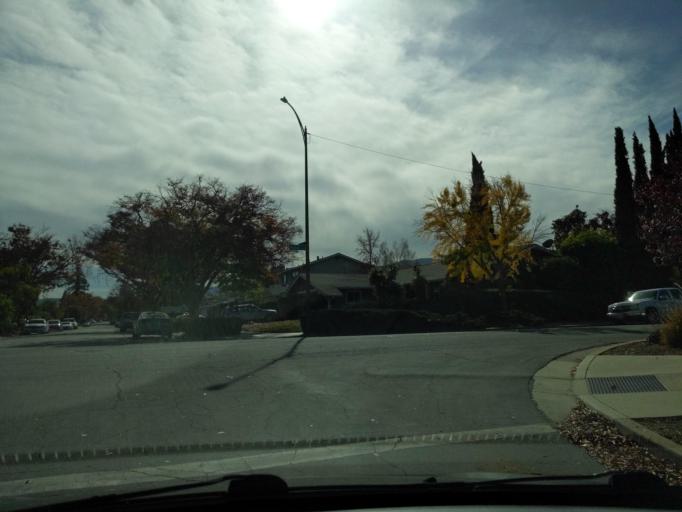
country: US
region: California
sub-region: Santa Clara County
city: Cambrian Park
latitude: 37.2495
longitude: -121.9056
